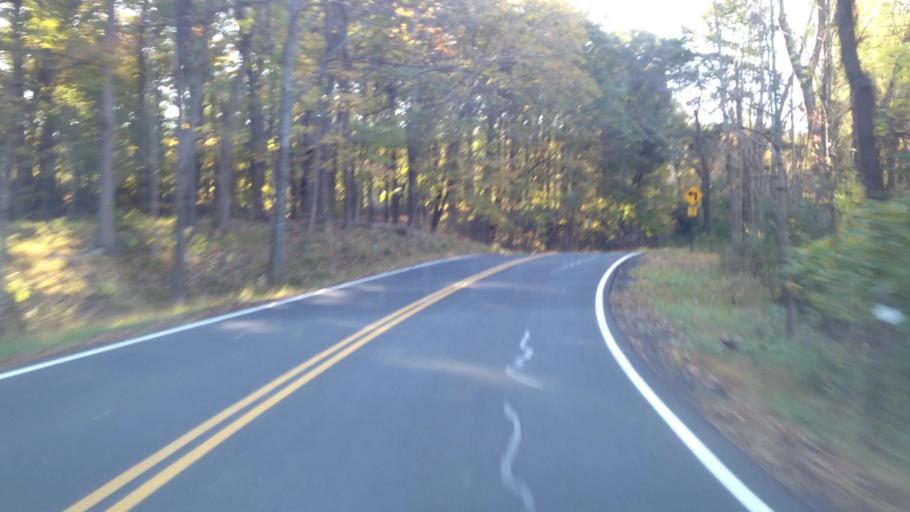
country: US
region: New York
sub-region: Dutchess County
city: Hyde Park
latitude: 41.8242
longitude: -73.9797
